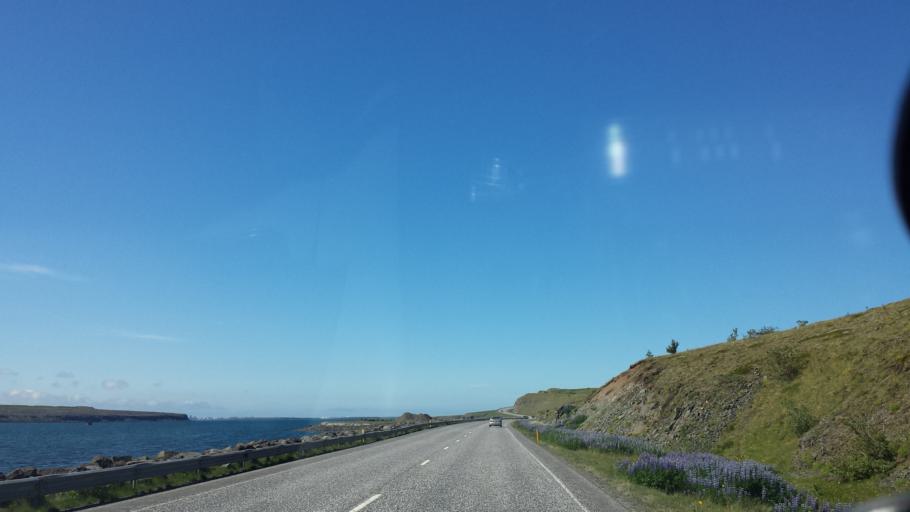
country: IS
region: Capital Region
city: Mosfellsbaer
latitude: 64.2079
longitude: -21.7280
